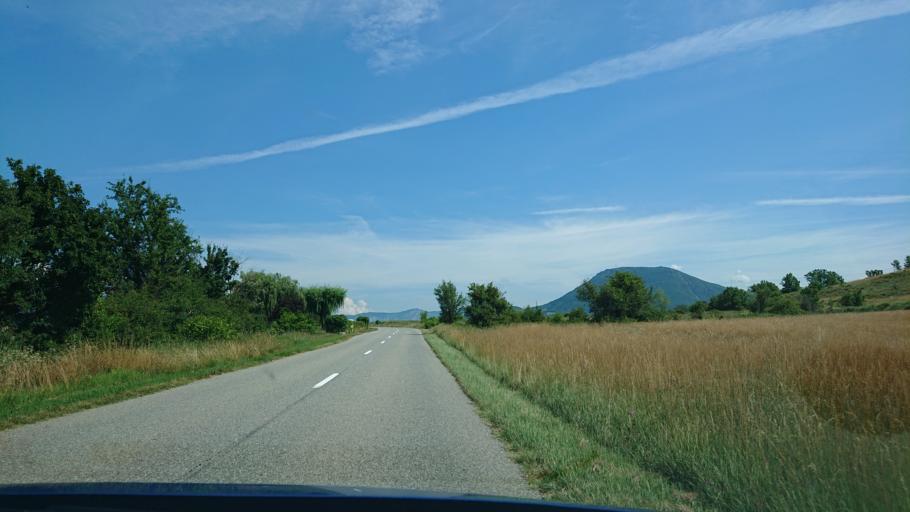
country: FR
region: Provence-Alpes-Cote d'Azur
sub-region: Departement des Alpes-de-Haute-Provence
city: Sisteron
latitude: 44.2401
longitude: 5.9478
